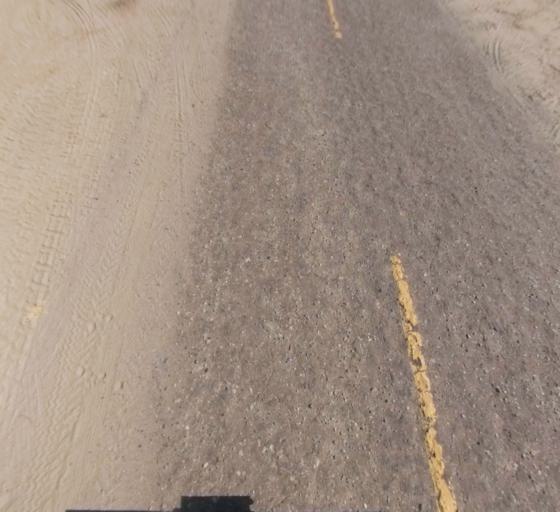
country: US
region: California
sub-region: Fresno County
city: Biola
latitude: 36.8437
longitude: -120.0464
